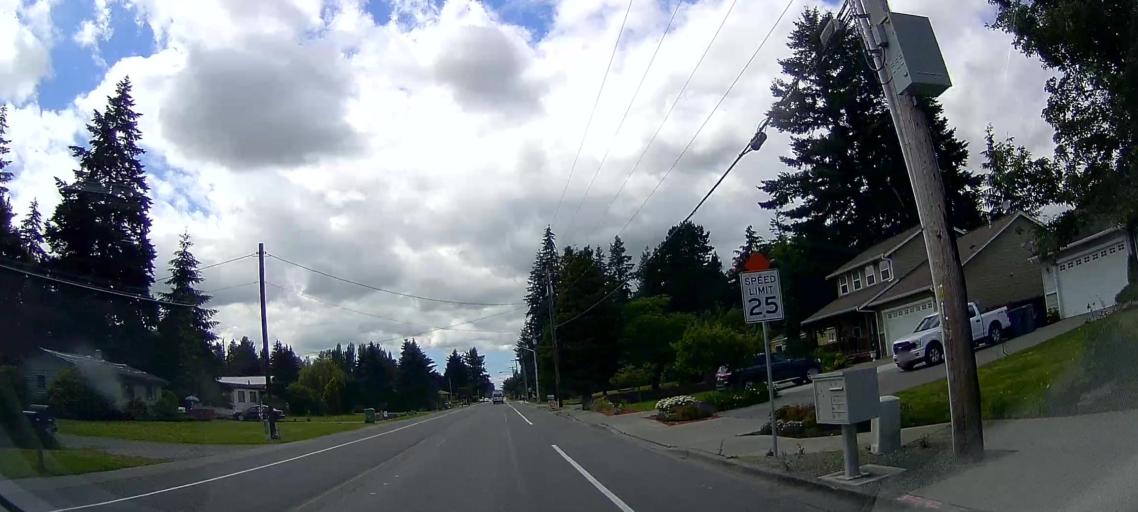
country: US
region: Washington
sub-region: Skagit County
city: Burlington
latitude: 48.4754
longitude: -122.3091
